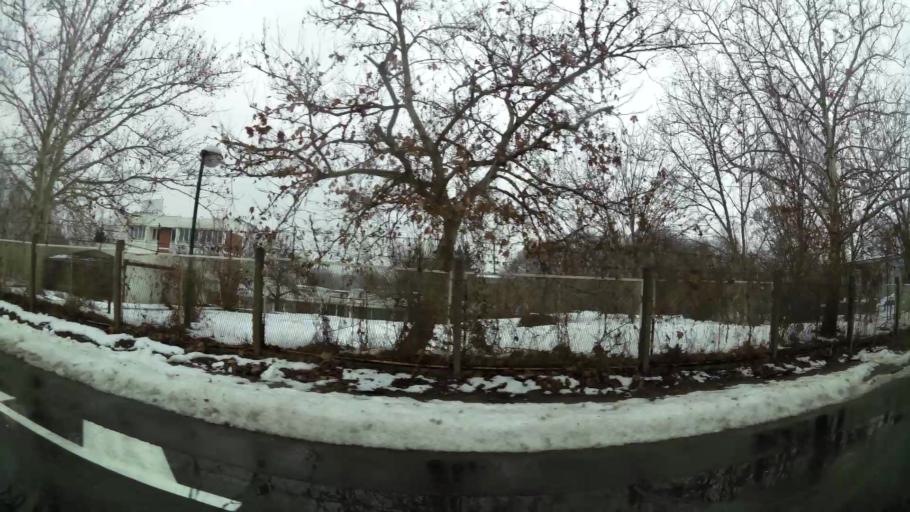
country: RS
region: Central Serbia
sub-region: Belgrade
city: Vozdovac
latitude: 44.7579
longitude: 20.4957
